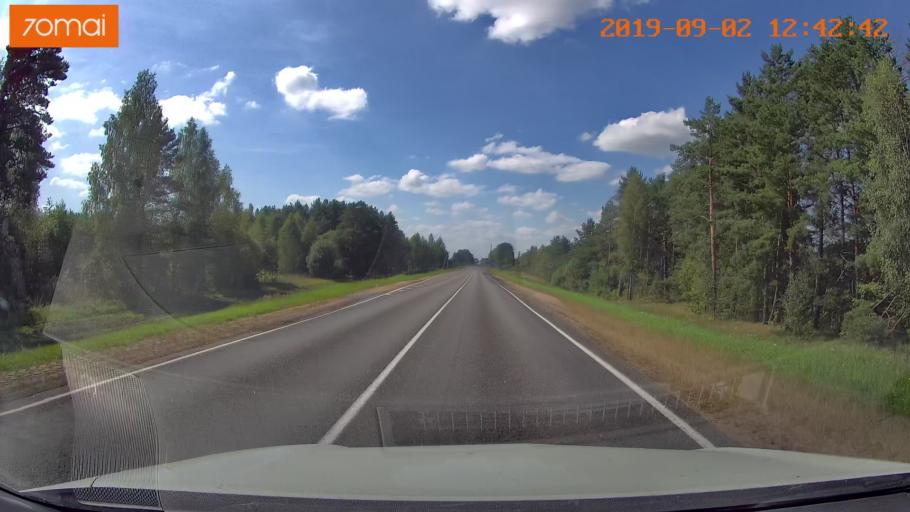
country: RU
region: Smolensk
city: Shumyachi
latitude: 53.7622
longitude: 32.2491
